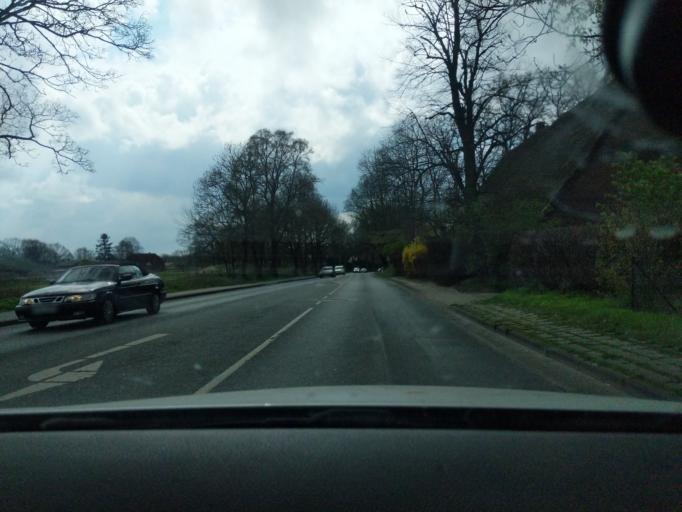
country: DE
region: Lower Saxony
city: Stade
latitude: 53.5809
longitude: 9.4719
